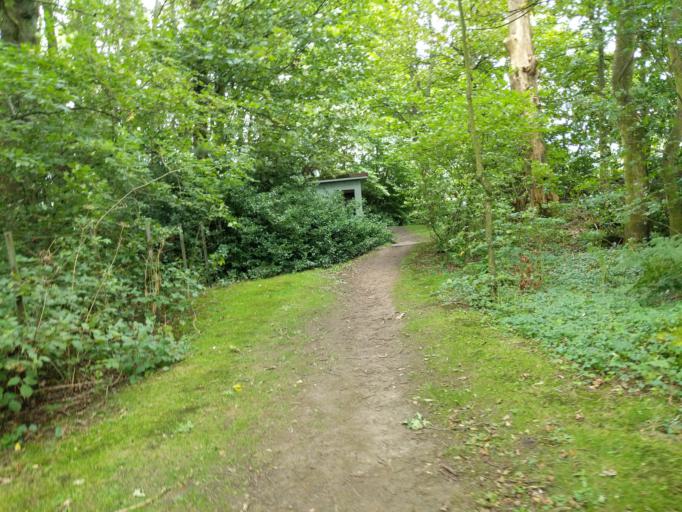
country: GB
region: Scotland
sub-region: Perth and Kinross
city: Kinross
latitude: 56.2012
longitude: -3.3928
